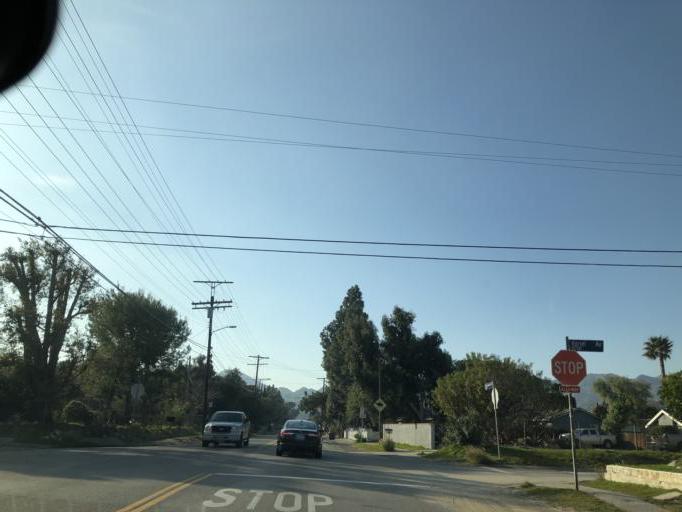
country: US
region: California
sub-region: Los Angeles County
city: Chatsworth
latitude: 34.2645
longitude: -118.5927
